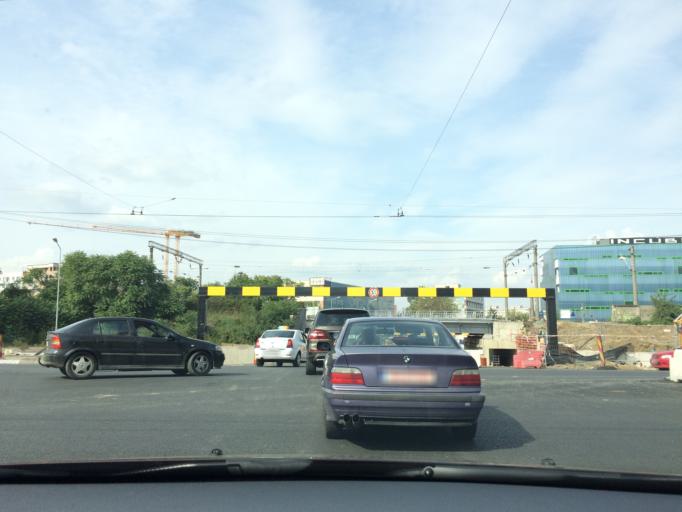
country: RO
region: Timis
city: Timisoara
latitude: 45.7516
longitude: 21.2162
